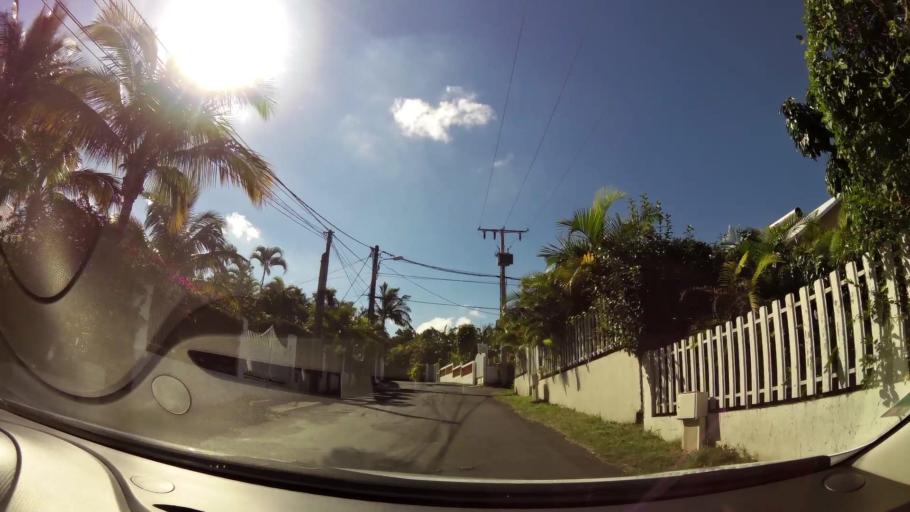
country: RE
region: Reunion
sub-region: Reunion
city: Le Tampon
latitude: -21.2702
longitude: 55.4991
